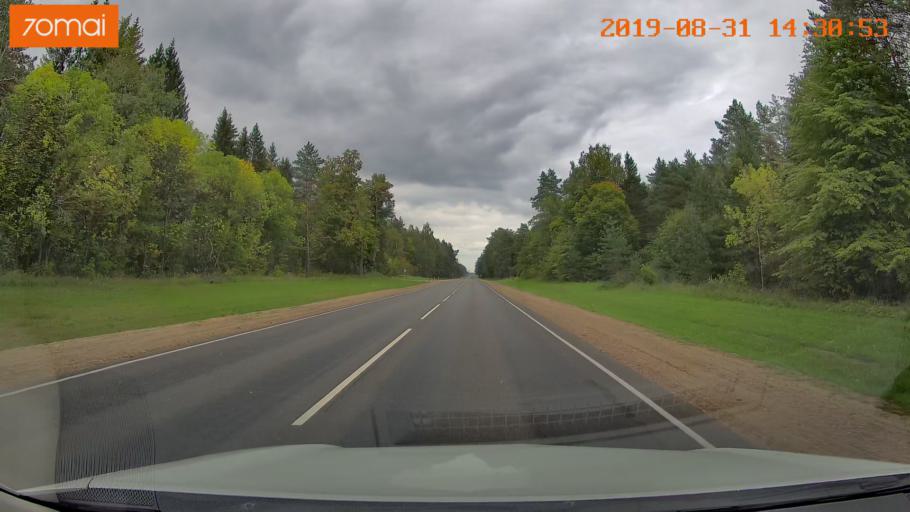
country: RU
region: Smolensk
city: Yekimovichi
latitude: 54.1346
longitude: 33.3610
